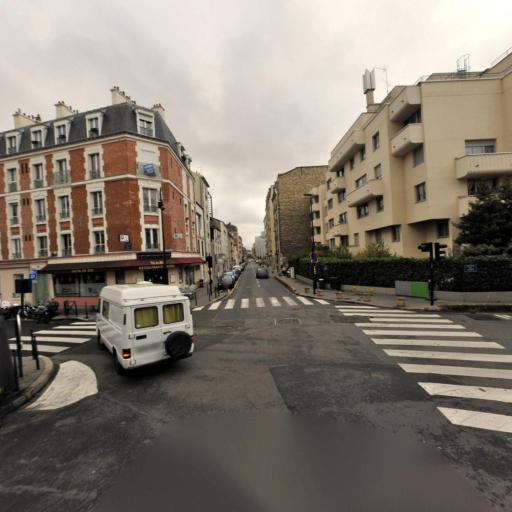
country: FR
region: Ile-de-France
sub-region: Departement des Hauts-de-Seine
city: Boulogne-Billancourt
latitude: 48.8377
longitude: 2.2479
